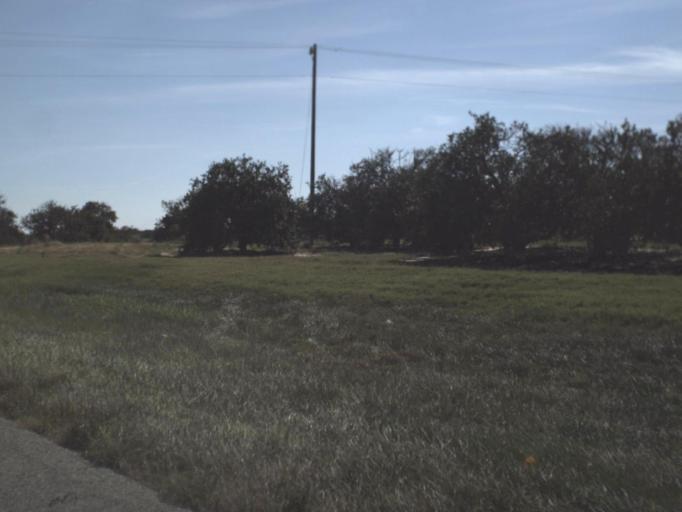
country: US
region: Florida
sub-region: Highlands County
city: Lake Placid
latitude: 27.2616
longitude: -81.3452
